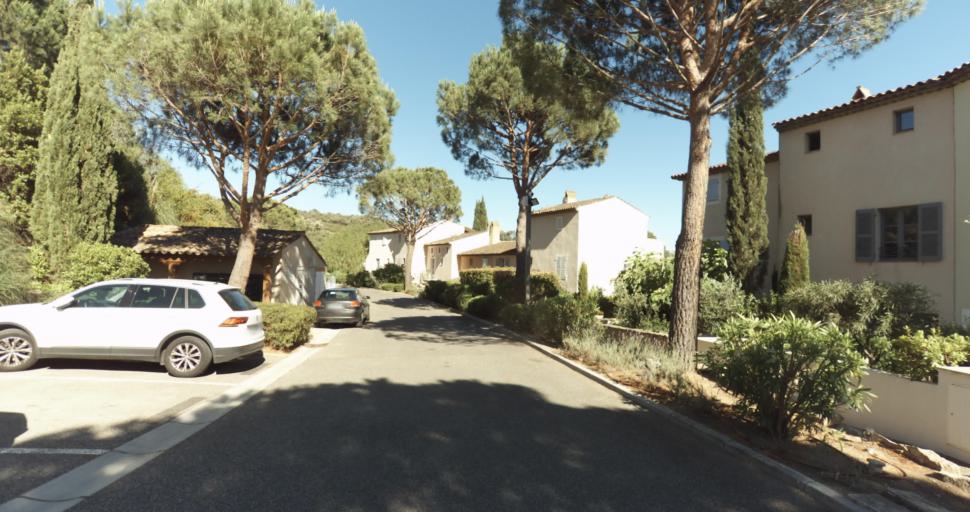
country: FR
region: Provence-Alpes-Cote d'Azur
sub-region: Departement du Var
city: Gassin
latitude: 43.2537
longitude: 6.6041
